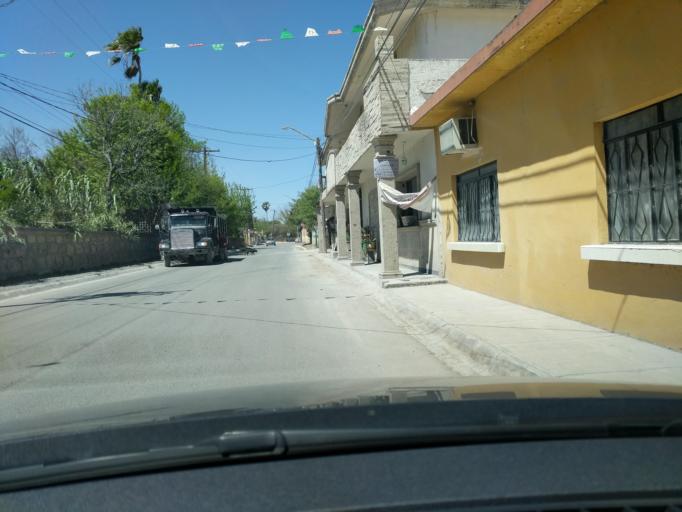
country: MX
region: Nuevo Leon
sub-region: Apodaca
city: Artemio Trevino
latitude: 25.8127
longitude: -100.1492
